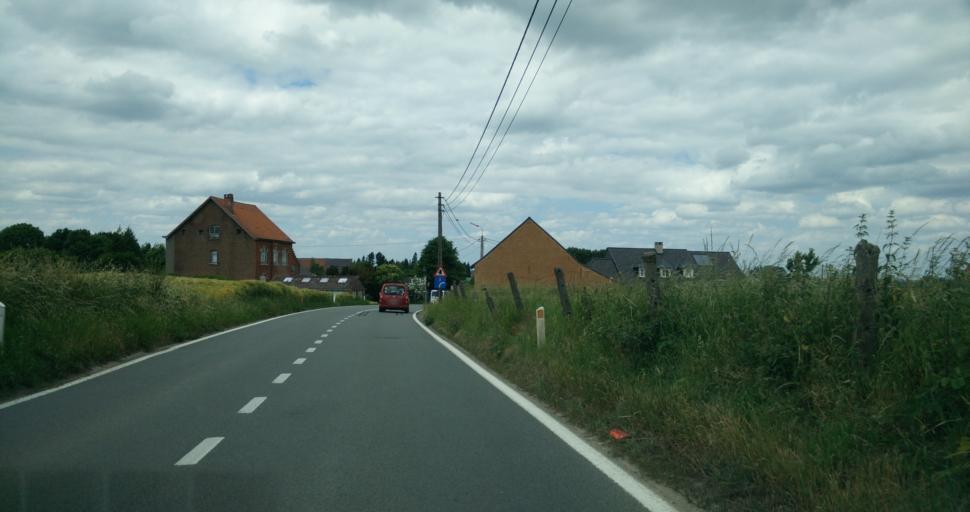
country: BE
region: Wallonia
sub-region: Province du Hainaut
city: Silly
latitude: 50.7079
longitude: 3.9304
